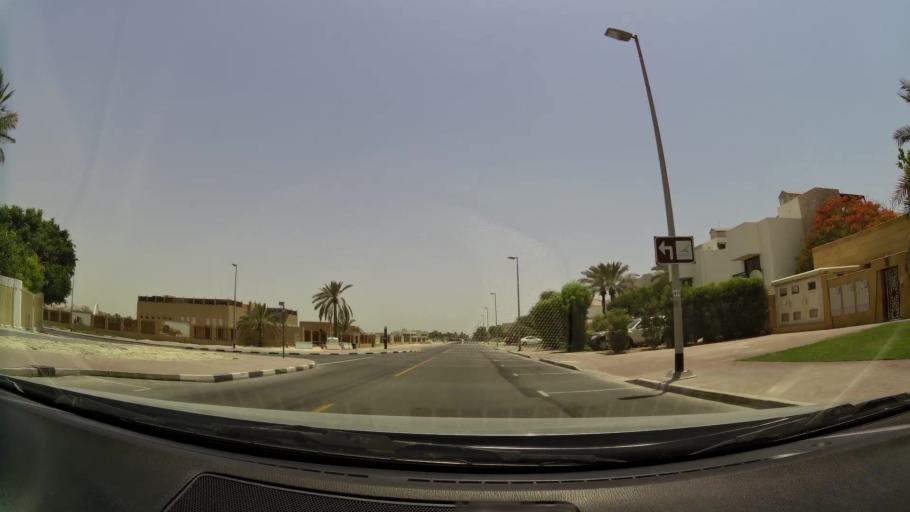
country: AE
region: Dubai
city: Dubai
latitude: 25.1991
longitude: 55.2416
